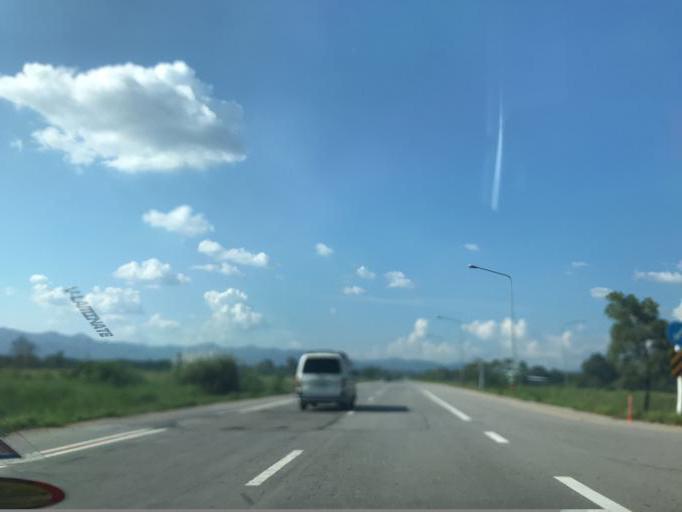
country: TH
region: Chiang Mai
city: San Pa Tong
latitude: 18.5866
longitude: 98.8392
